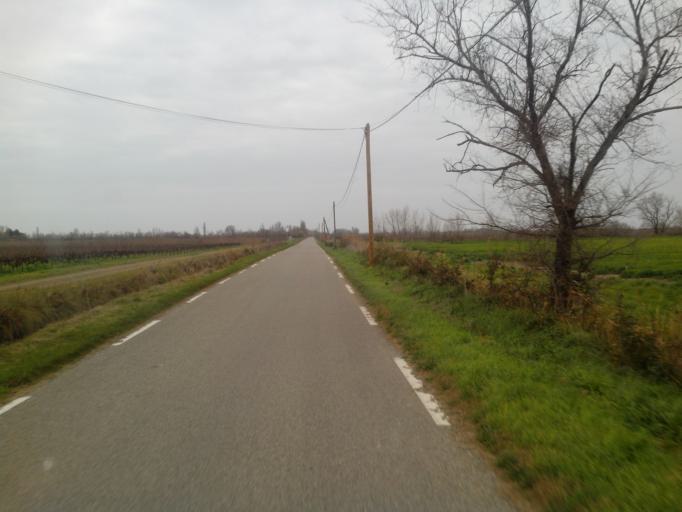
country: FR
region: Languedoc-Roussillon
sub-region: Departement du Gard
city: Vauvert
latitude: 43.5741
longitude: 4.3310
